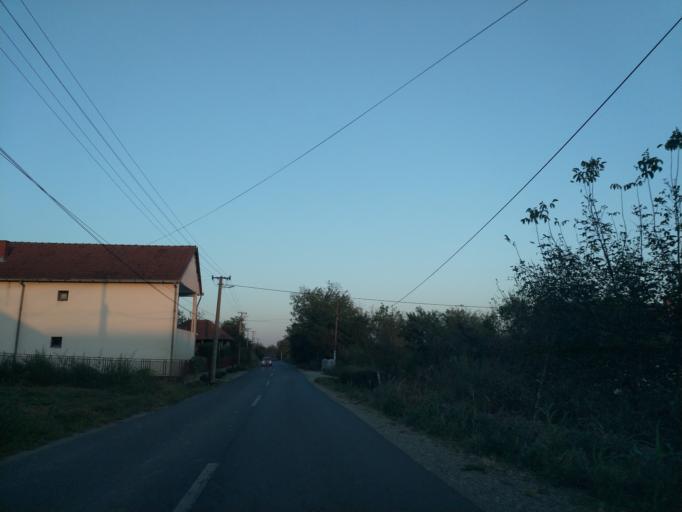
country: RS
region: Central Serbia
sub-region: Rasinski Okrug
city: Krusevac
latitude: 43.6043
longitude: 21.2444
